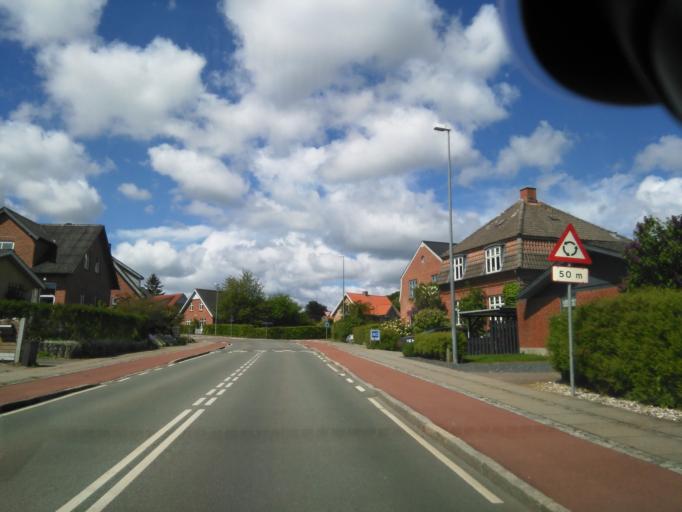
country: DK
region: Central Jutland
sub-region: Odder Kommune
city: Odder
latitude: 55.9720
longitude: 10.1369
